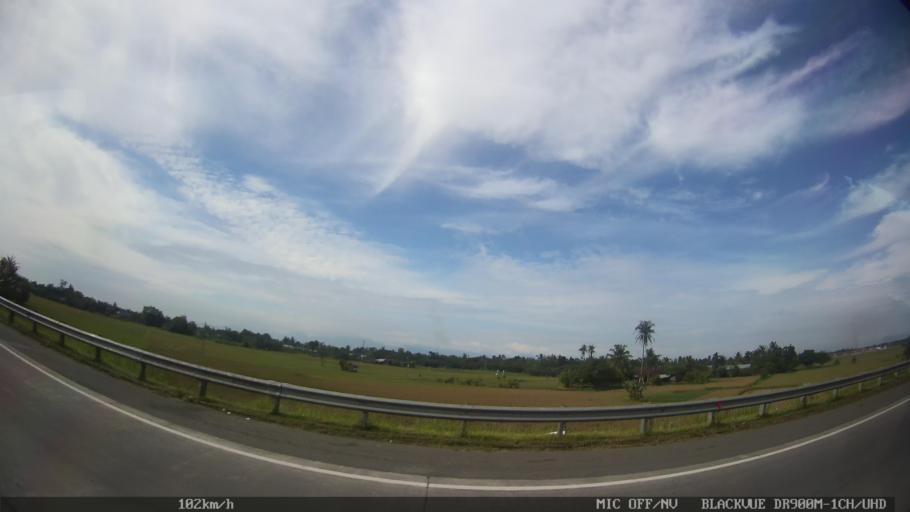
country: ID
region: North Sumatra
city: Sunggal
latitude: 3.6409
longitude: 98.5695
